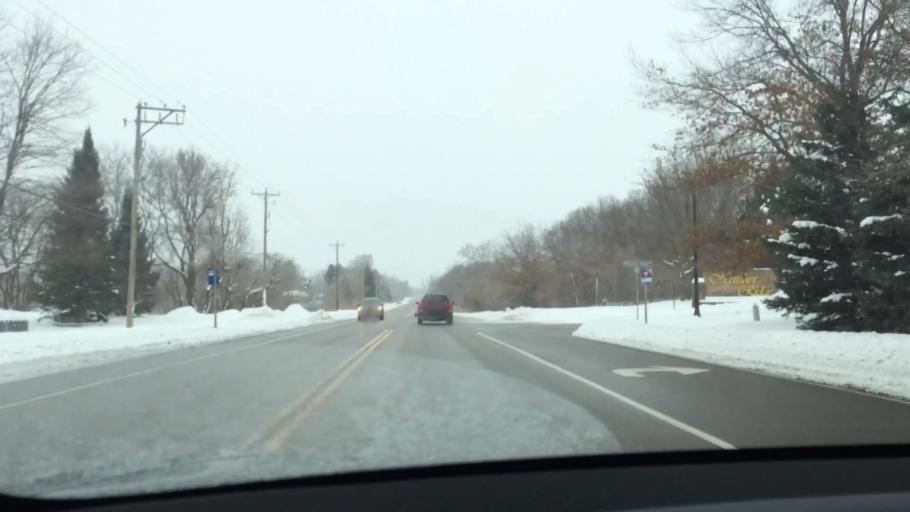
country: US
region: Minnesota
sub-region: Ramsey County
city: Shoreview
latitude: 45.1115
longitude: -93.1273
